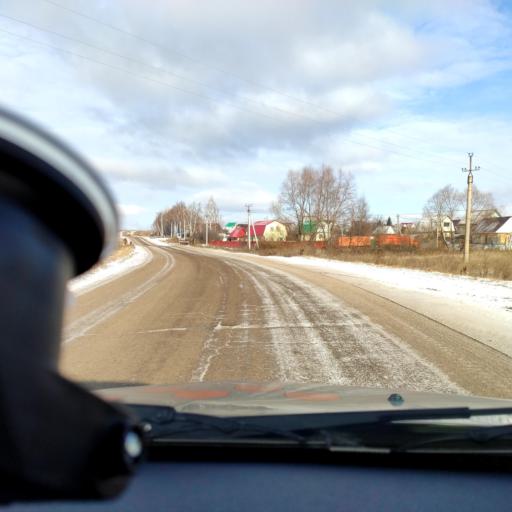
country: RU
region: Bashkortostan
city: Mikhaylovka
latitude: 54.7984
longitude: 55.7799
